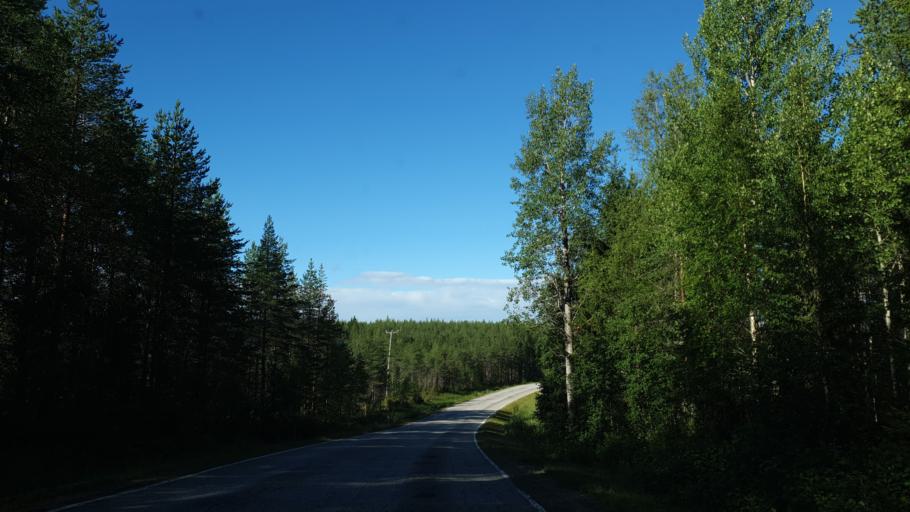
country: FI
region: Kainuu
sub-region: Kehys-Kainuu
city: Kuhmo
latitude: 64.3185
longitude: 29.4779
